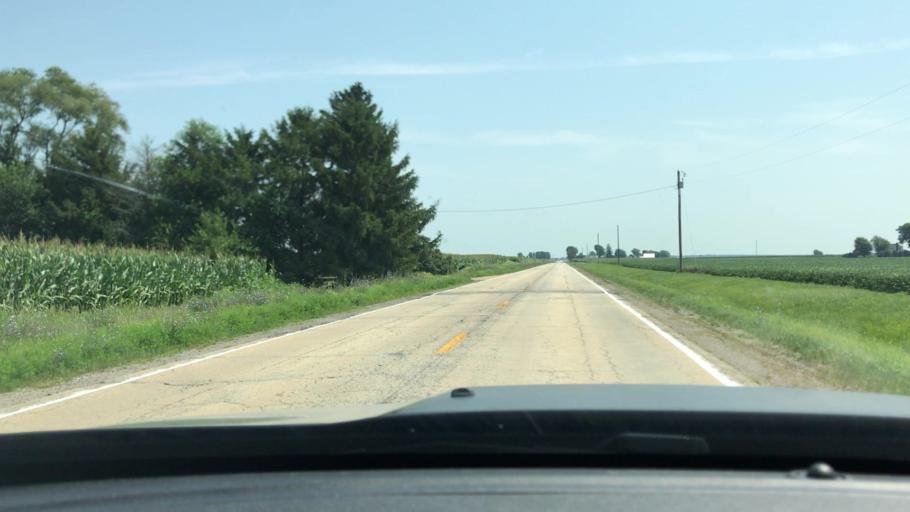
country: US
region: Illinois
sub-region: LaSalle County
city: Ottawa
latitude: 41.4702
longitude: -88.8578
